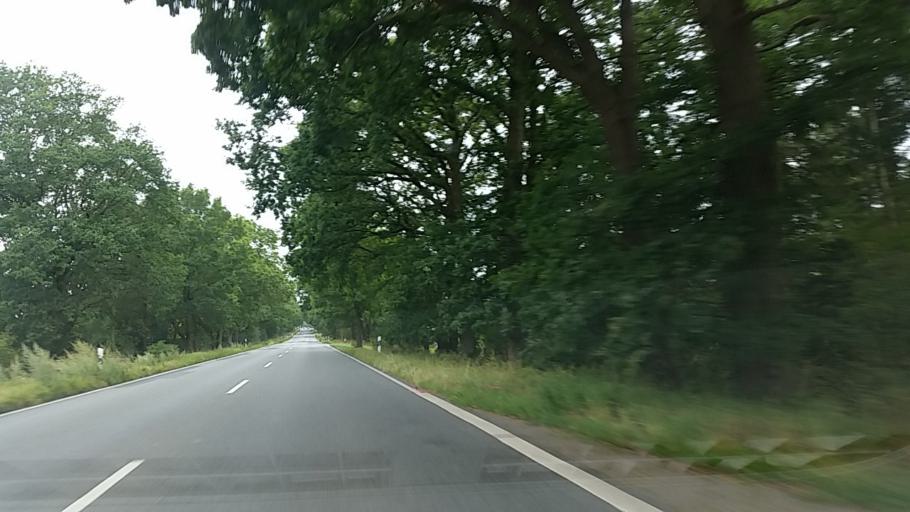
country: DE
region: Lower Saxony
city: Loxstedt
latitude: 53.4797
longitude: 8.6970
